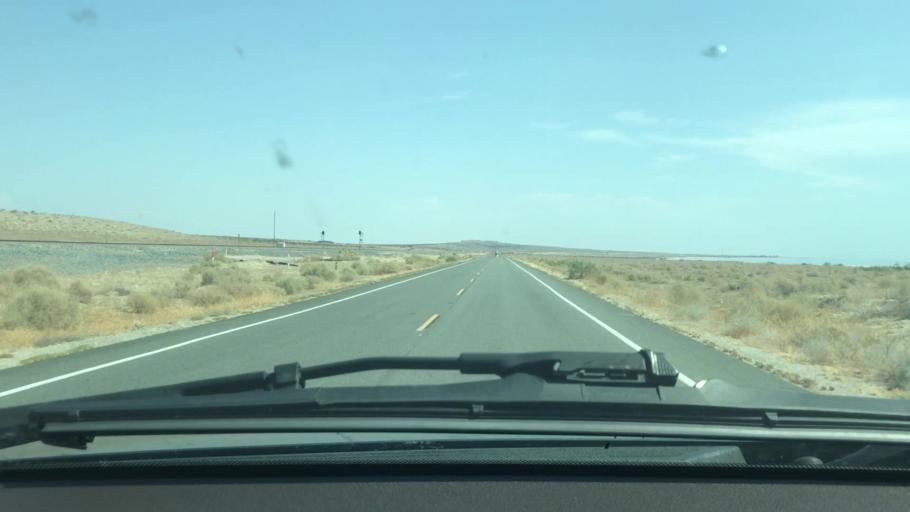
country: US
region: California
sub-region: Imperial County
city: Desert Shores
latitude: 33.4641
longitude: -115.8709
